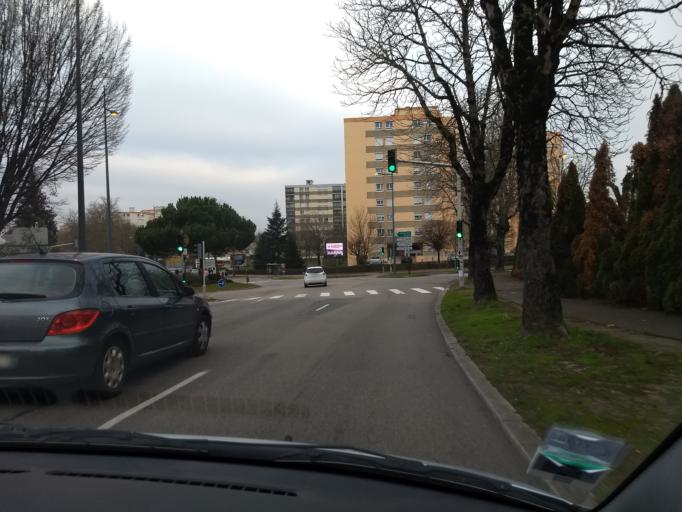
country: FR
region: Limousin
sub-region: Departement de la Haute-Vienne
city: Isle
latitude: 45.8271
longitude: 1.2265
